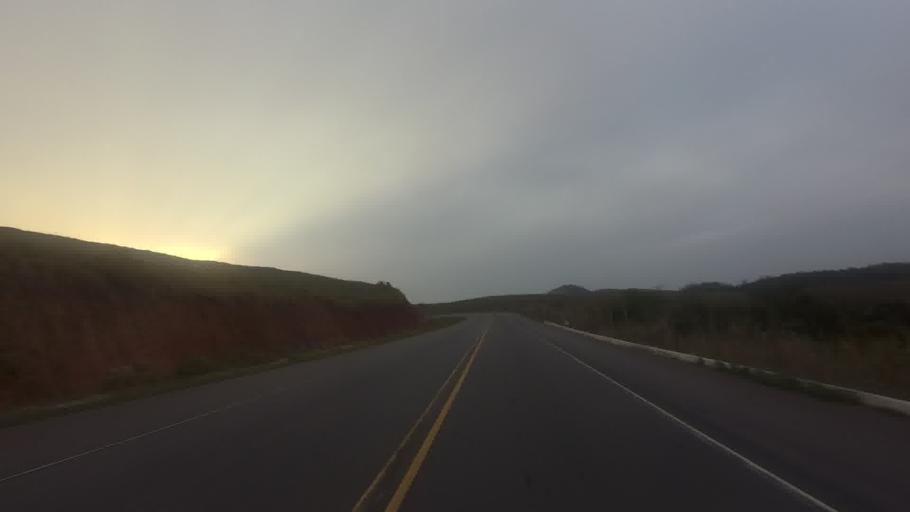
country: BR
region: Minas Gerais
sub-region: Recreio
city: Recreio
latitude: -21.7479
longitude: -42.4675
